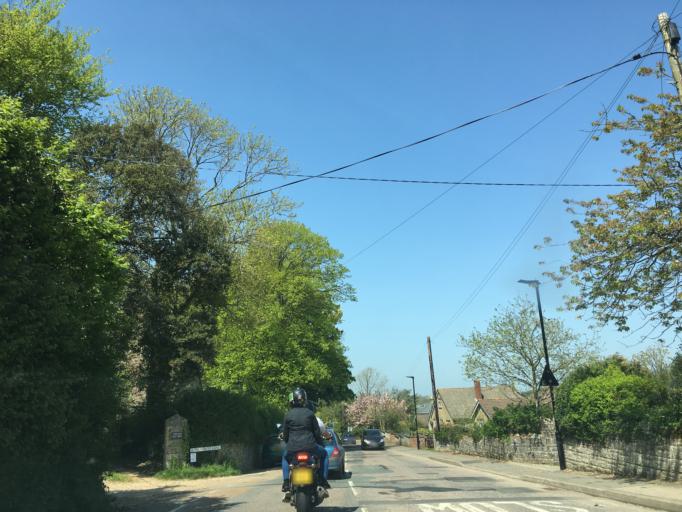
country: GB
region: England
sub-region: Isle of Wight
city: Niton
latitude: 50.5963
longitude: -1.2633
